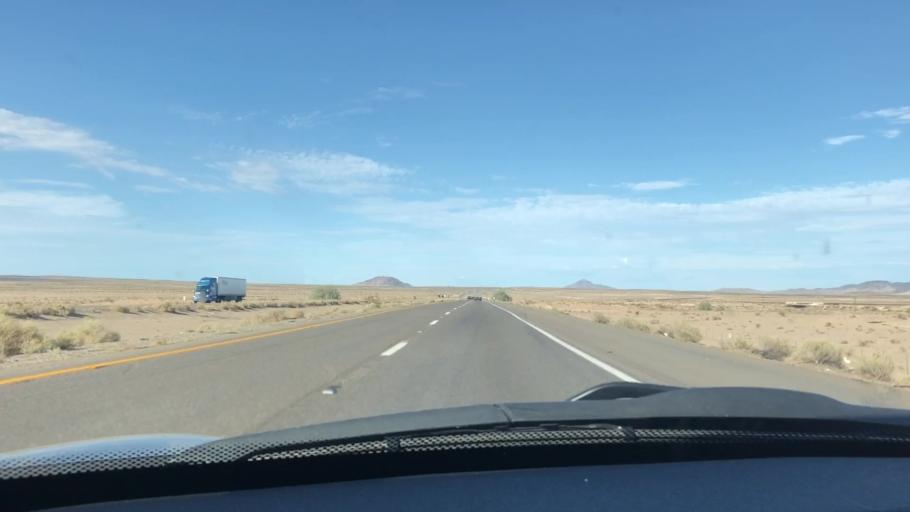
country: US
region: California
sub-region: San Bernardino County
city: Fort Irwin
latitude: 34.9898
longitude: -116.5845
